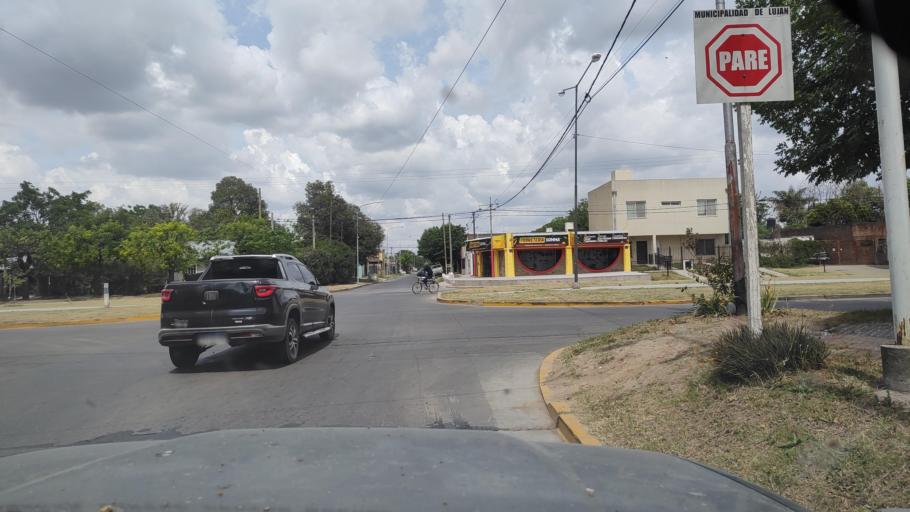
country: AR
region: Buenos Aires
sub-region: Partido de Lujan
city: Lujan
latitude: -34.5600
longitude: -59.1278
